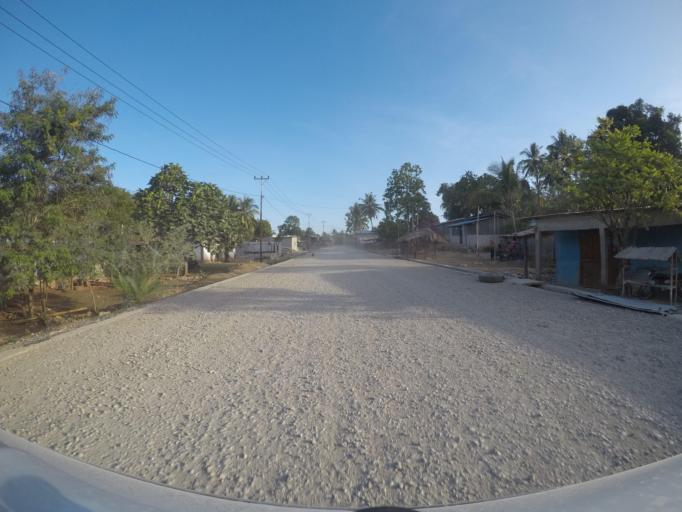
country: TL
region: Viqueque
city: Viqueque
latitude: -8.8350
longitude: 126.5190
